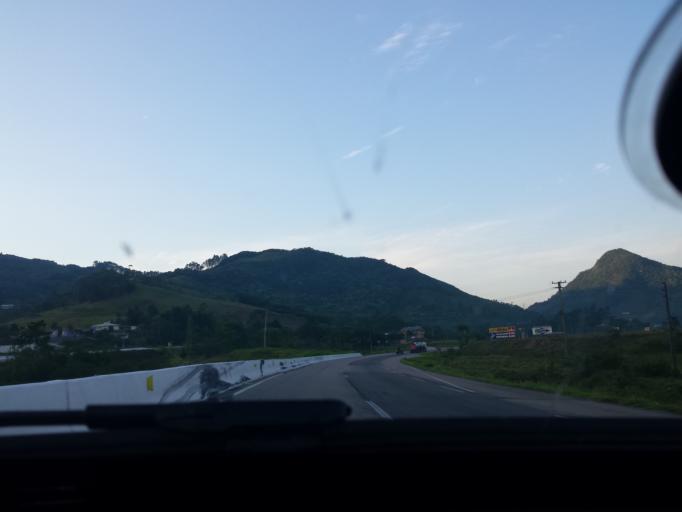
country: BR
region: Santa Catarina
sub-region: Imbituba
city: Imbituba
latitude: -27.9871
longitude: -48.6795
